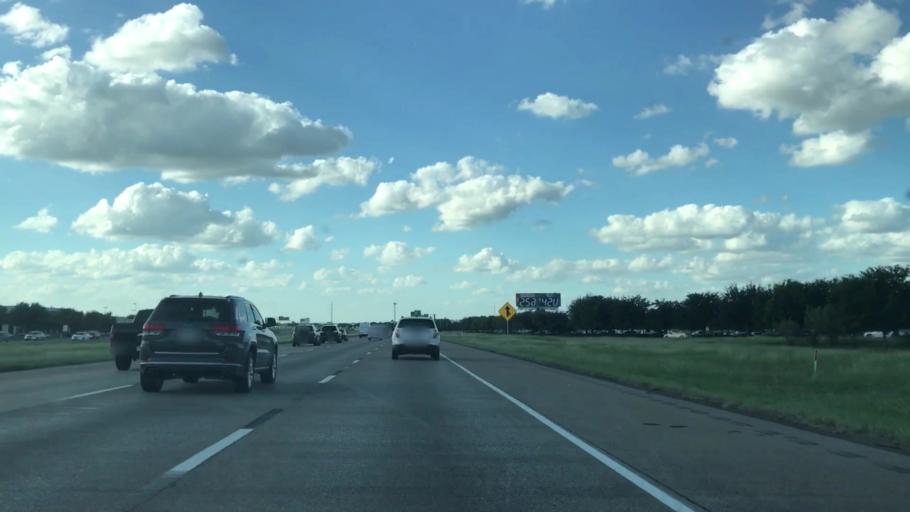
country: US
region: Texas
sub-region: Dallas County
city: Coppell
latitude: 32.9364
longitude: -97.0091
